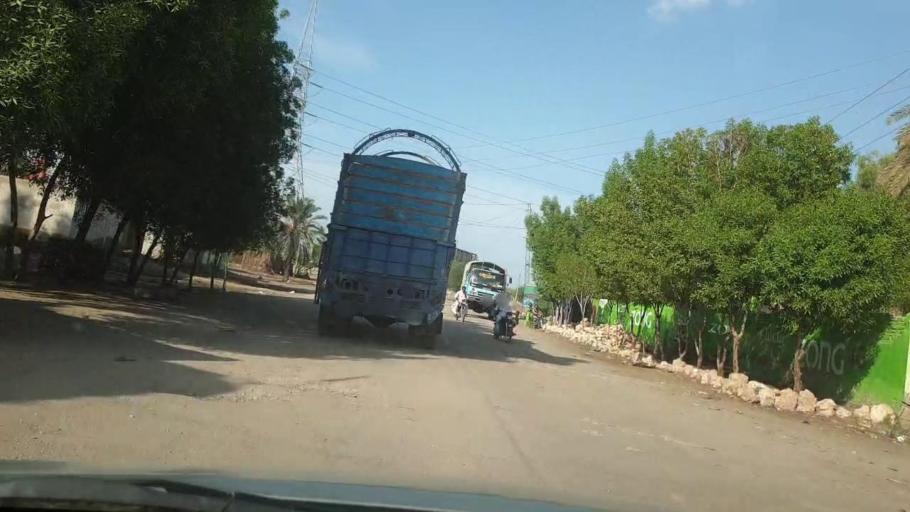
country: PK
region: Sindh
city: Sukkur
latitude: 27.6634
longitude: 68.8456
